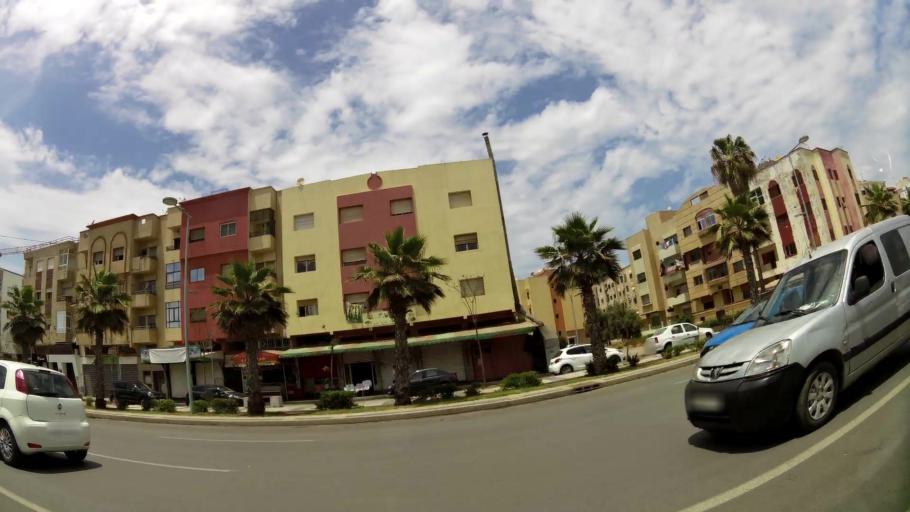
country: MA
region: Rabat-Sale-Zemmour-Zaer
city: Sale
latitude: 34.0573
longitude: -6.8059
